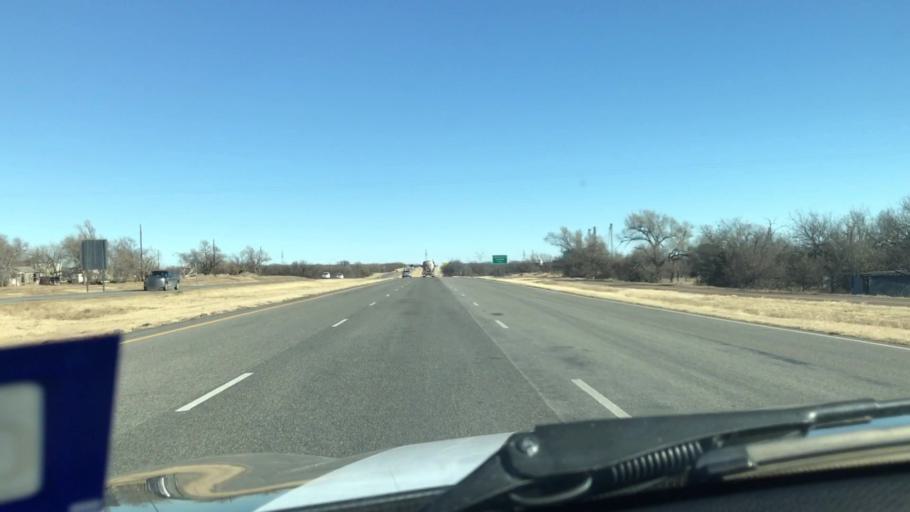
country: US
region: Texas
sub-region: Scurry County
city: Snyder
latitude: 32.6879
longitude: -100.8535
